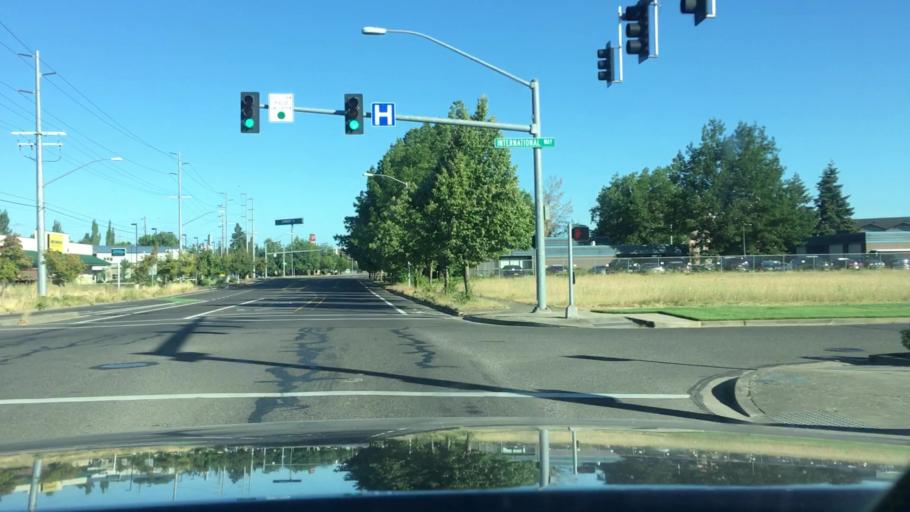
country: US
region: Oregon
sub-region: Lane County
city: Springfield
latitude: 44.0873
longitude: -123.0442
